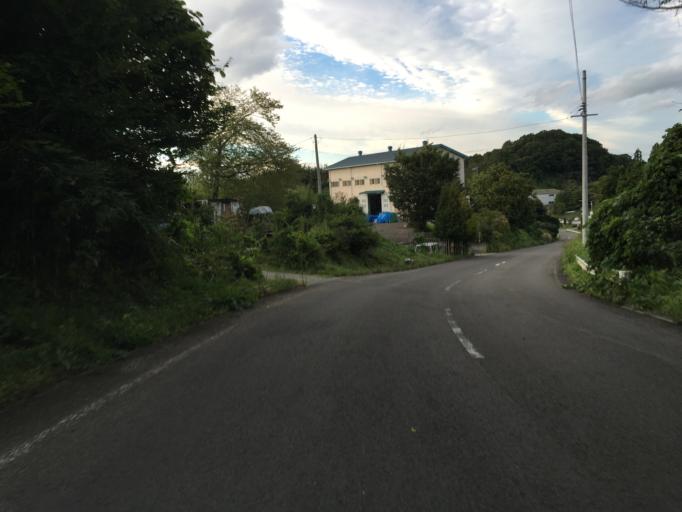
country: JP
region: Fukushima
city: Nihommatsu
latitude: 37.6292
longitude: 140.4965
